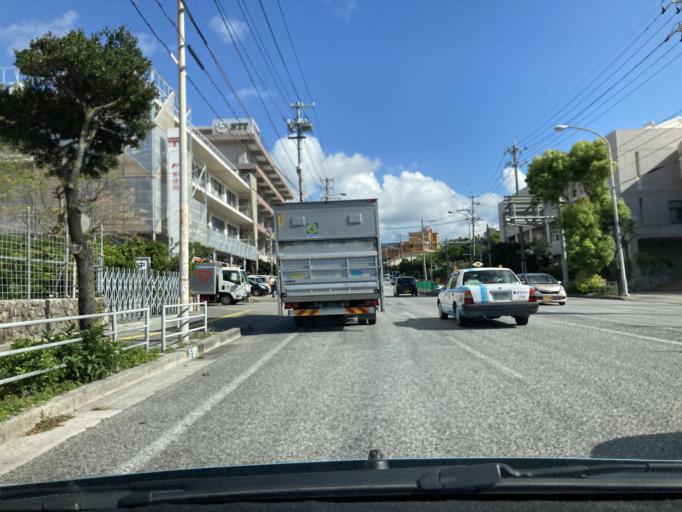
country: JP
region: Okinawa
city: Naha-shi
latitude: 26.2071
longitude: 127.6935
